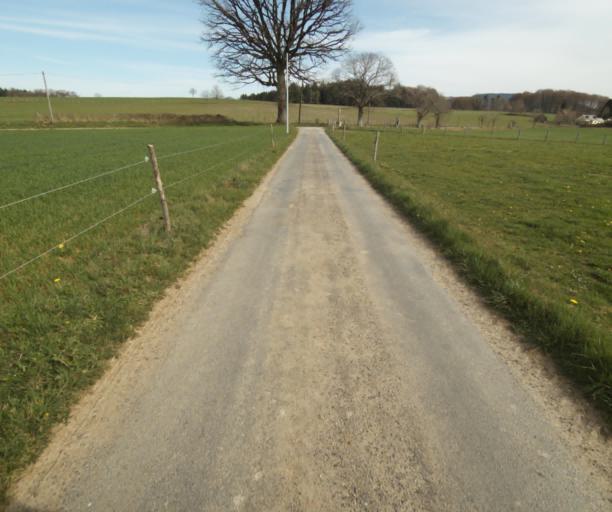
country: FR
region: Limousin
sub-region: Departement de la Correze
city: Correze
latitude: 45.4170
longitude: 1.8205
